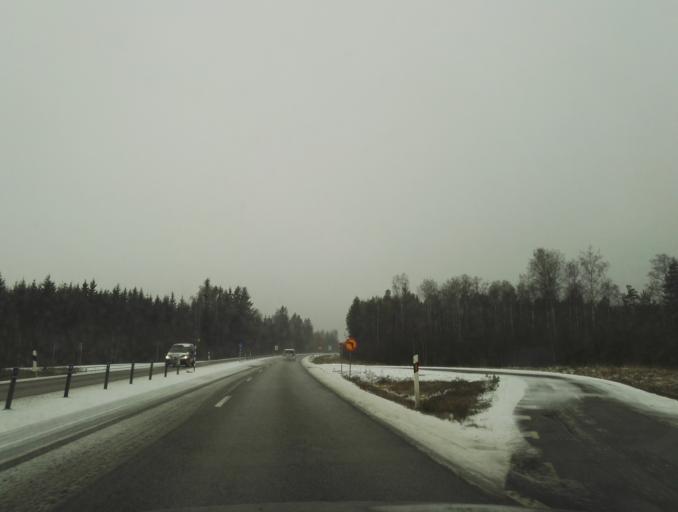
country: SE
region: Kronoberg
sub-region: Alvesta Kommun
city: Vislanda
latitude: 56.7544
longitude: 14.5209
